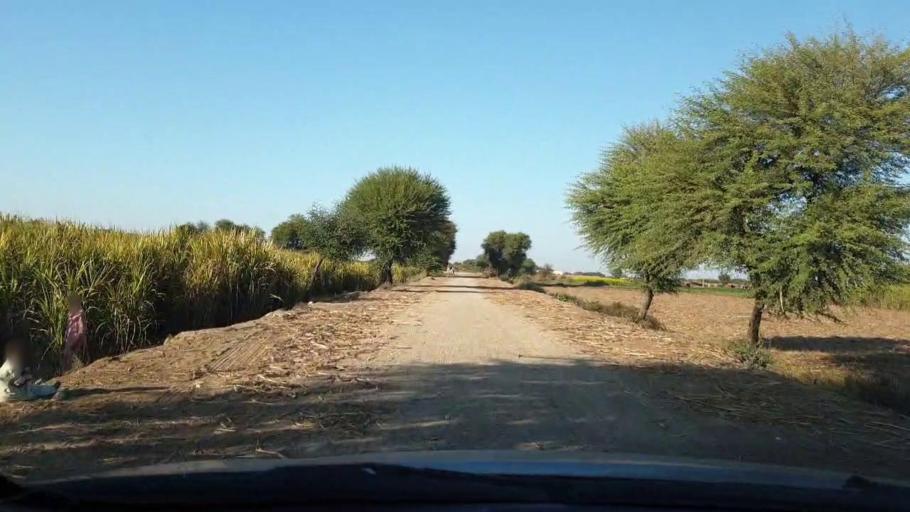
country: PK
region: Sindh
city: Jhol
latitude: 25.8939
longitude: 68.9476
